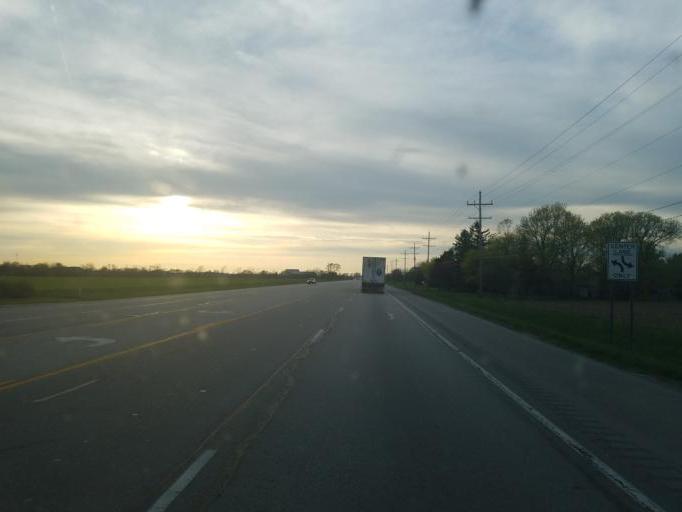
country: US
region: Ohio
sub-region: Sandusky County
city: Woodville
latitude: 41.4575
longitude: -83.3803
